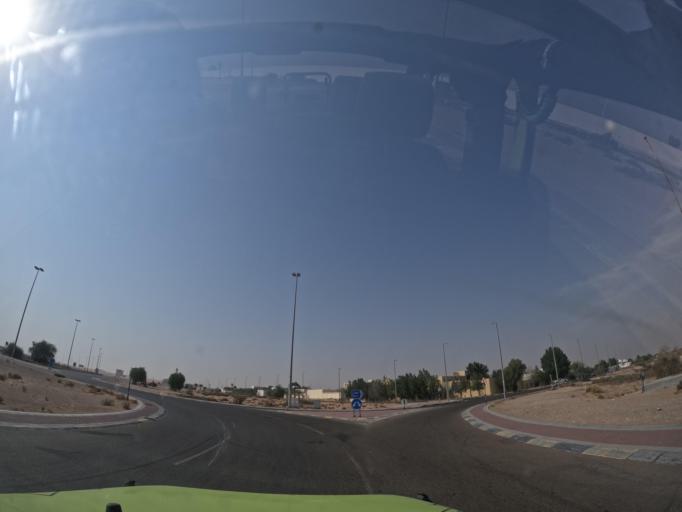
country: OM
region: Al Buraimi
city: Al Buraymi
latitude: 24.5245
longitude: 55.5528
